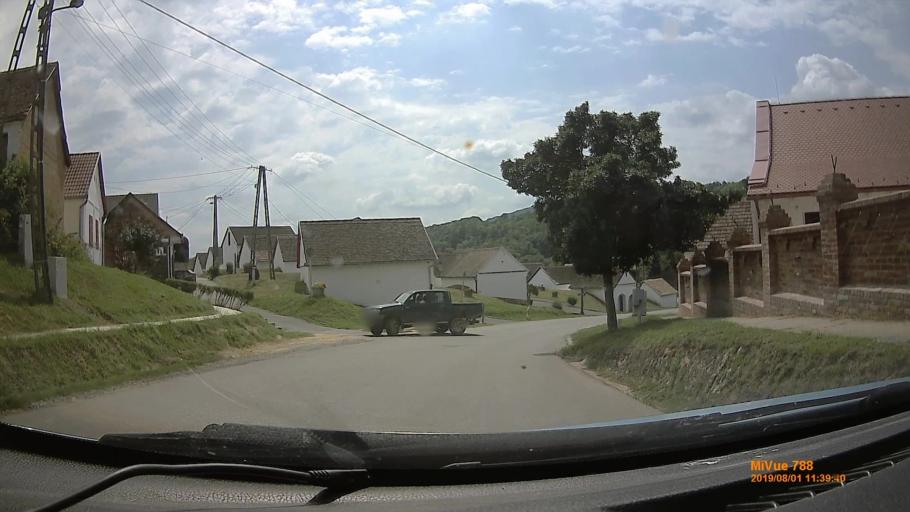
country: HU
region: Baranya
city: Villany
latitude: 45.8935
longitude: 18.3931
